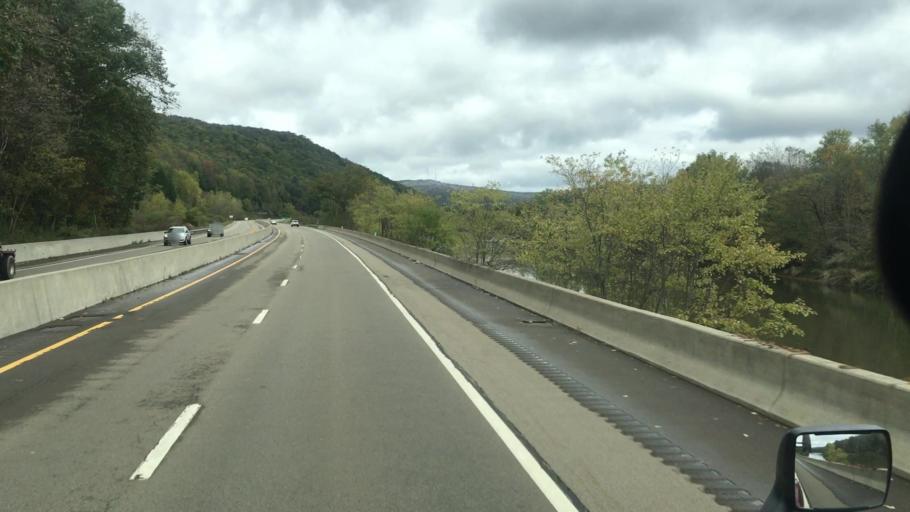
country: US
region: New York
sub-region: Cattaraugus County
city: Salamanca
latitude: 42.1192
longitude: -78.6638
